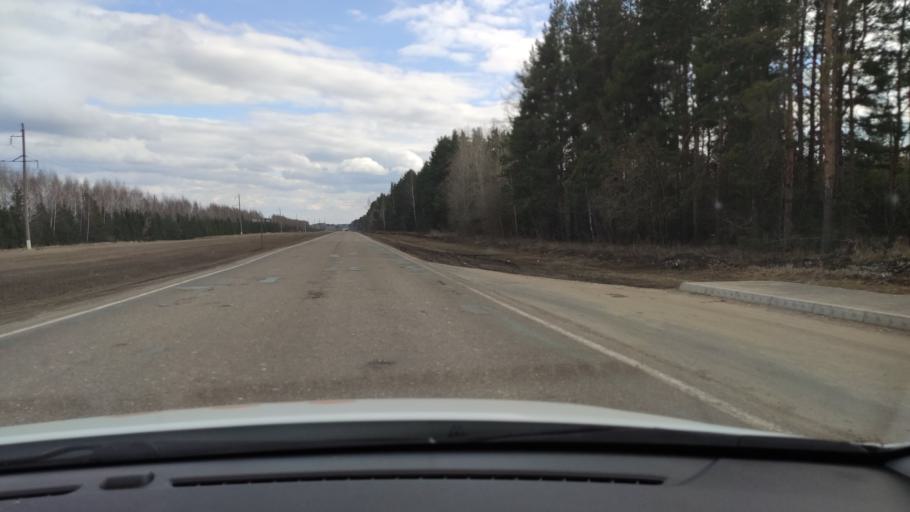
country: RU
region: Tatarstan
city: Vysokaya Gora
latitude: 56.0565
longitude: 49.2085
